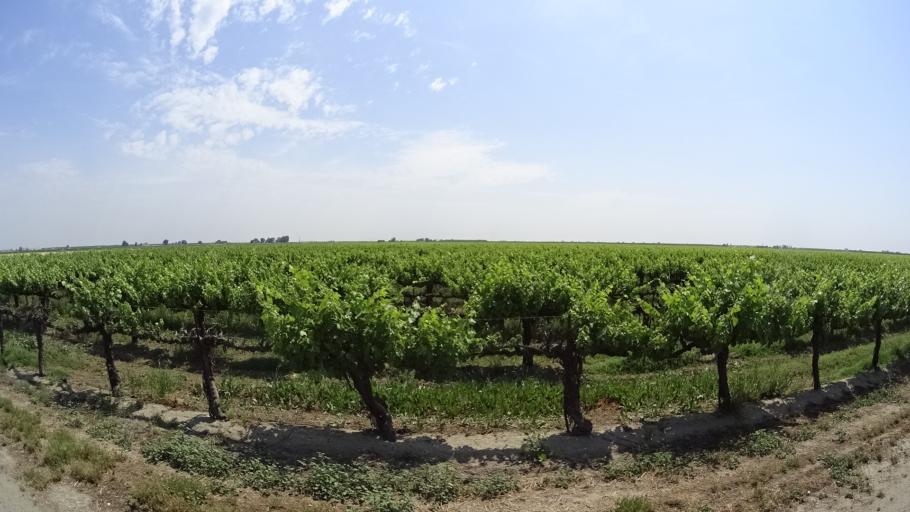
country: US
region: California
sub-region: Kings County
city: Lemoore
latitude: 36.3564
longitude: -119.7629
